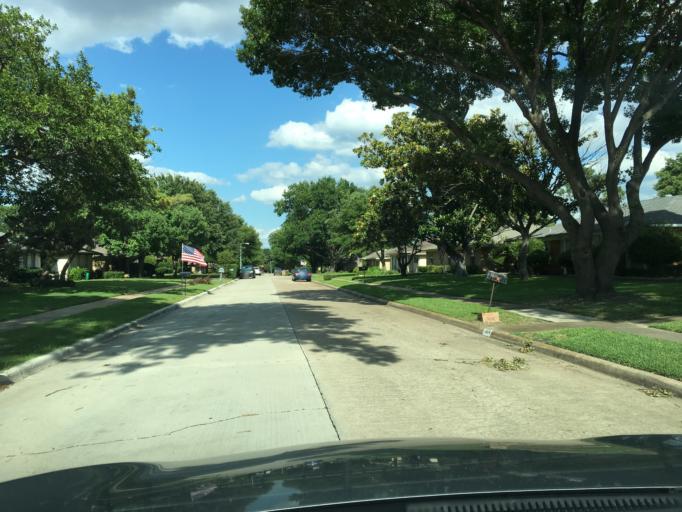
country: US
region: Texas
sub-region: Dallas County
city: Richardson
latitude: 32.9459
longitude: -96.6907
